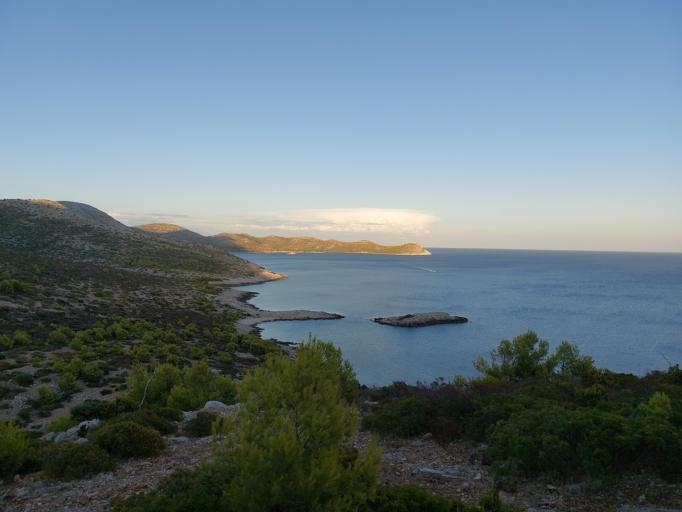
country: HR
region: Dubrovacko-Neretvanska
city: Smokvica
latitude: 42.7314
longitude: 16.8415
